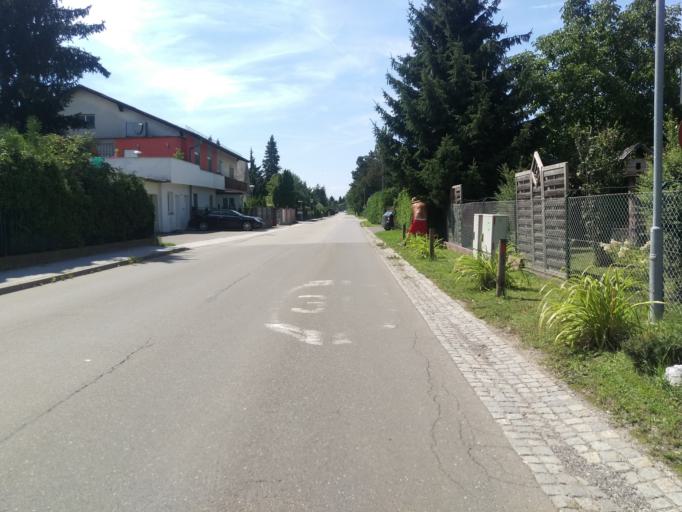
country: AT
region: Styria
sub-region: Politischer Bezirk Graz-Umgebung
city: Feldkirchen bei Graz
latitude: 47.0095
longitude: 15.4292
